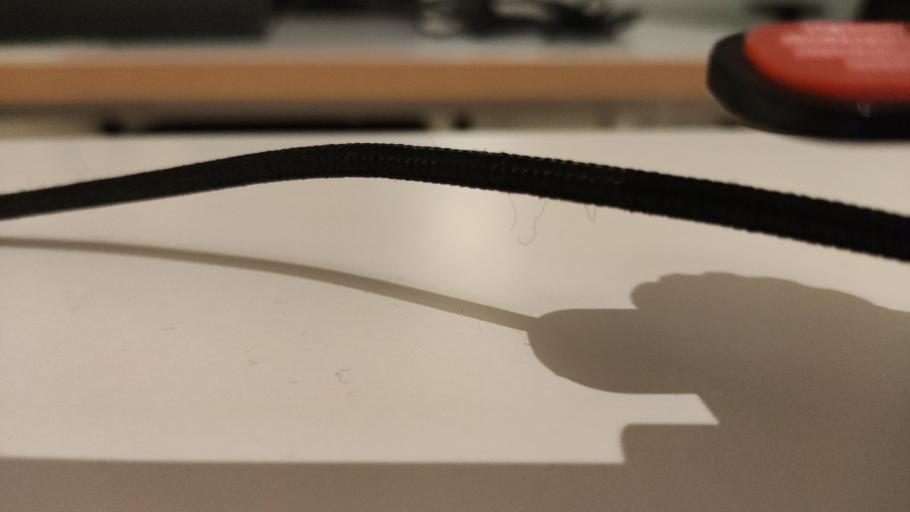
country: RU
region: Moskovskaya
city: Ol'yavidovo
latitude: 56.4300
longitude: 37.8146
